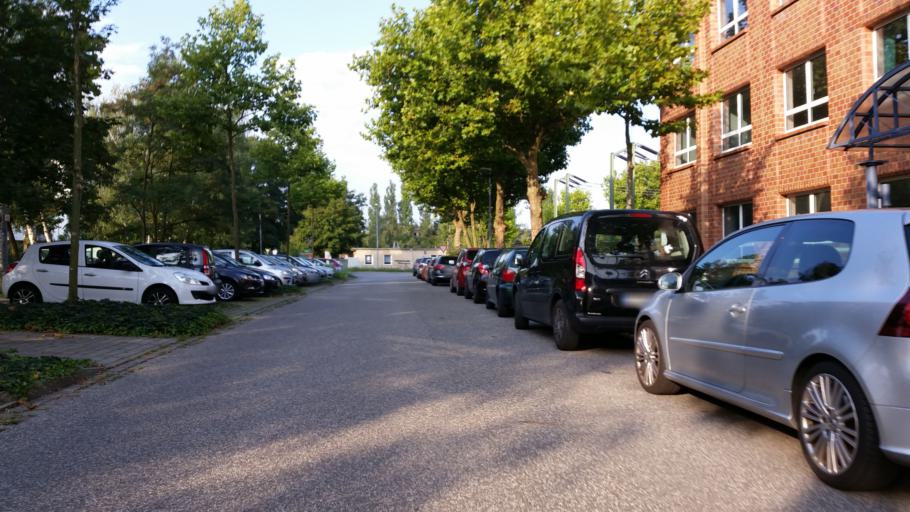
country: DE
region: Brandenburg
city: Teltow
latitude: 52.4023
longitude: 13.2526
